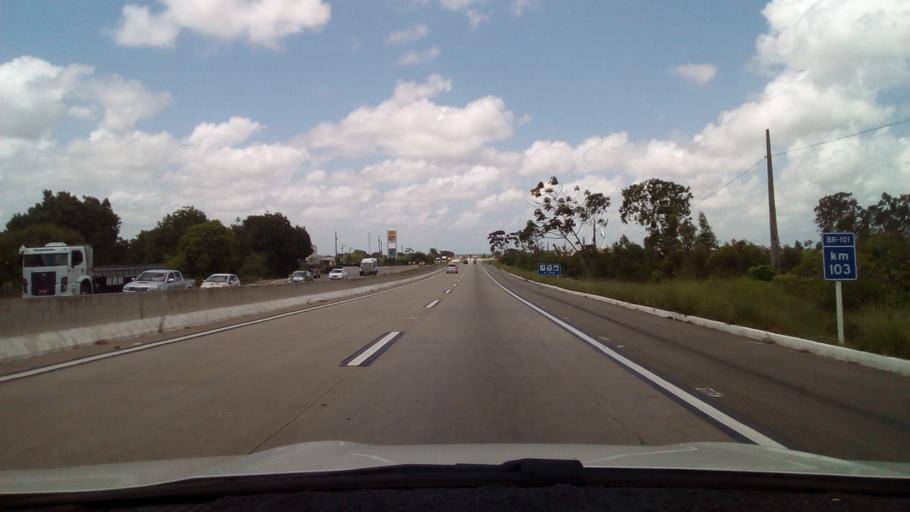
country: BR
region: Paraiba
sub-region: Conde
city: Conde
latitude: -7.2921
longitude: -34.9378
